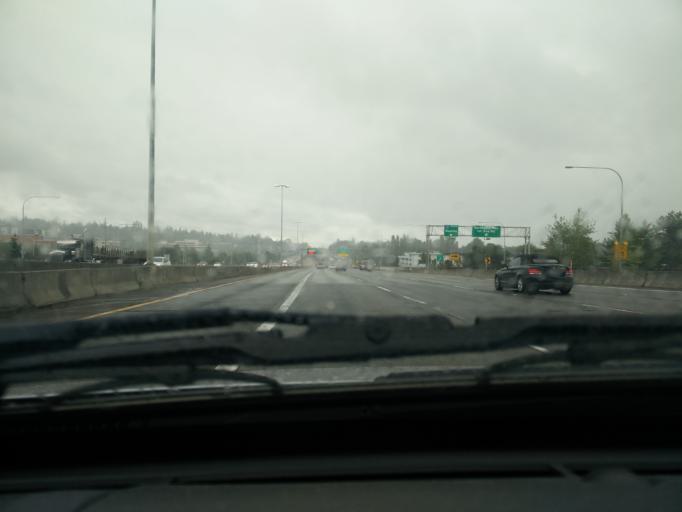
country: US
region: Washington
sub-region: King County
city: Shoreline
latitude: 47.7087
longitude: -122.3301
